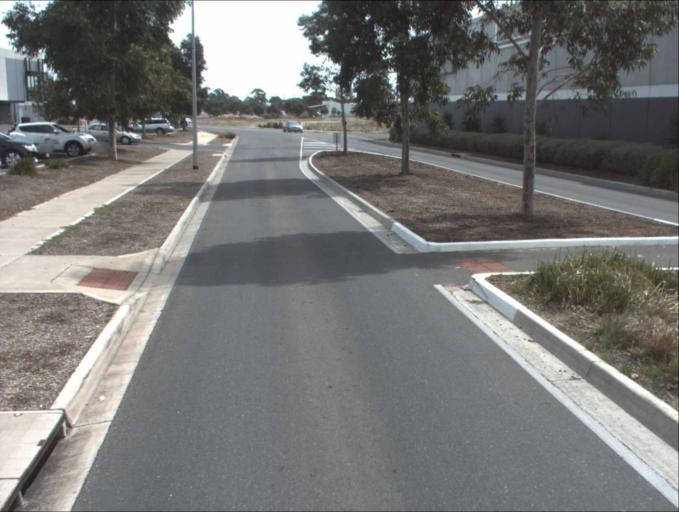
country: AU
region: South Australia
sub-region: Port Adelaide Enfield
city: Enfield
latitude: -34.8369
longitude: 138.6053
